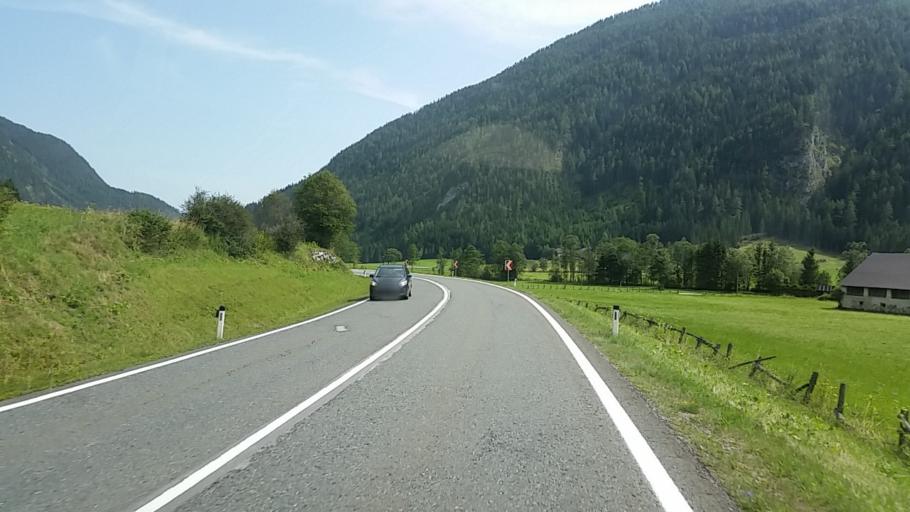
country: AT
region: Salzburg
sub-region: Politischer Bezirk Tamsweg
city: Tweng
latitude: 47.1771
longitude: 13.6297
